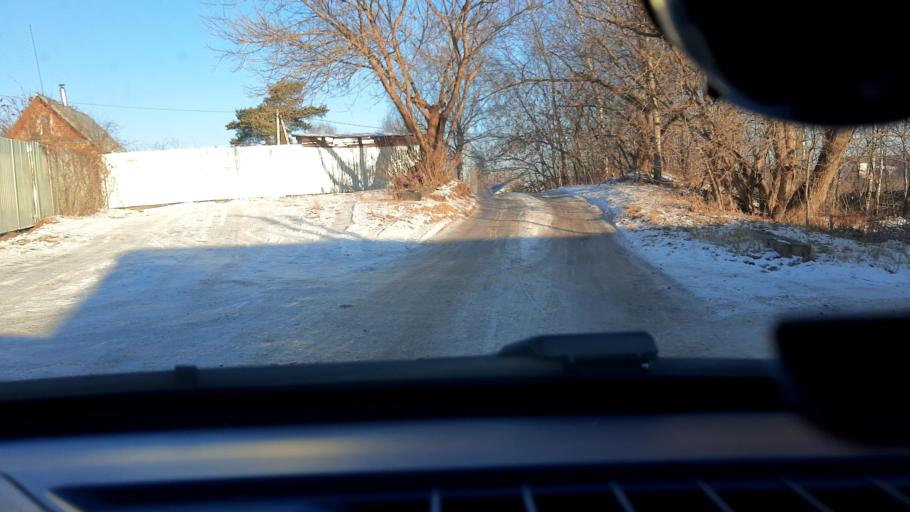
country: RU
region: Nizjnij Novgorod
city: Gorbatovka
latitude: 56.3312
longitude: 43.8193
